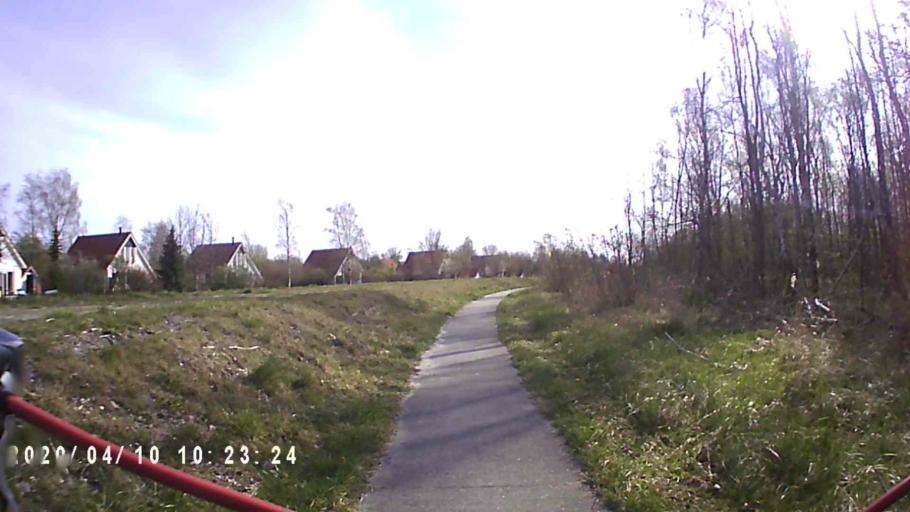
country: NL
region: Friesland
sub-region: Gemeente Dongeradeel
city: Anjum
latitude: 53.3853
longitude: 6.2154
